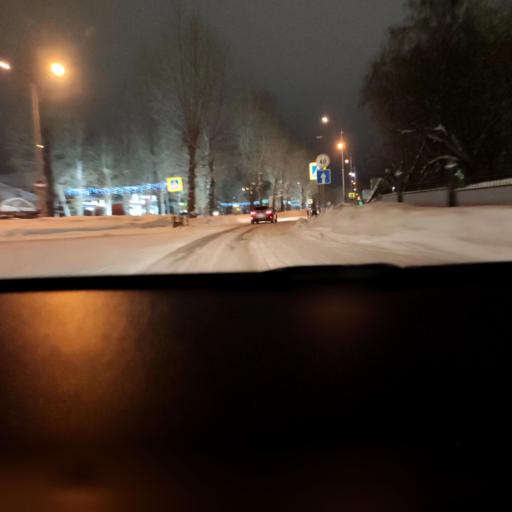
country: RU
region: Tatarstan
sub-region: Chistopol'skiy Rayon
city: Chistopol'
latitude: 55.3614
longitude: 50.6473
